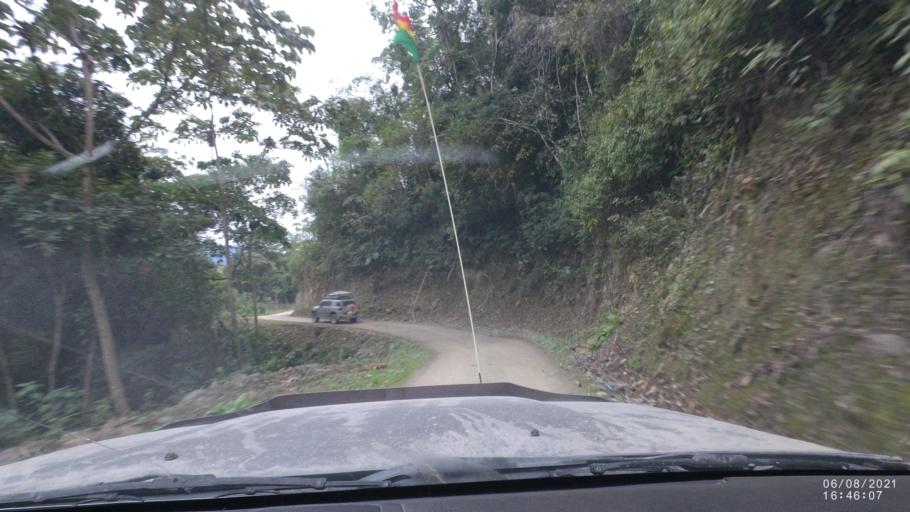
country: BO
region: La Paz
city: Quime
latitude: -16.5060
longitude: -66.7590
